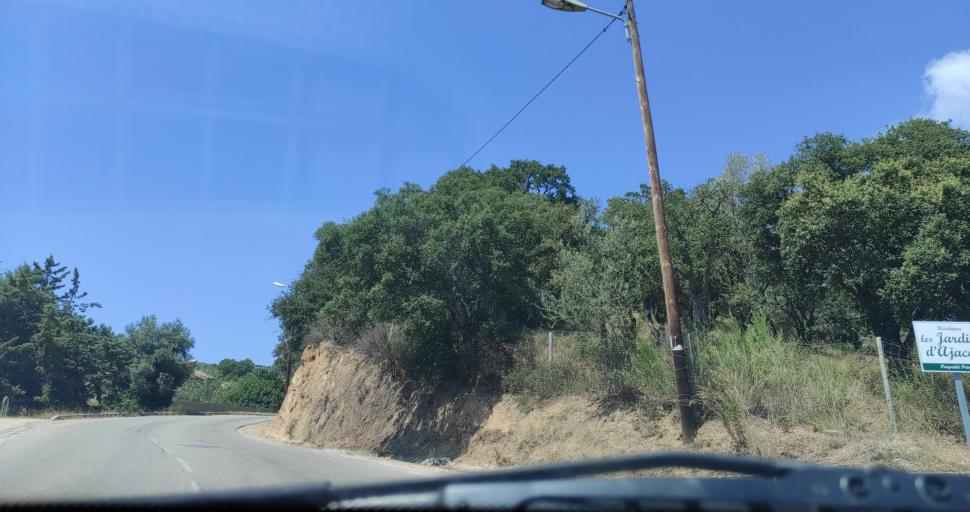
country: FR
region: Corsica
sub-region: Departement de la Corse-du-Sud
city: Ajaccio
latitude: 41.9463
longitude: 8.7372
